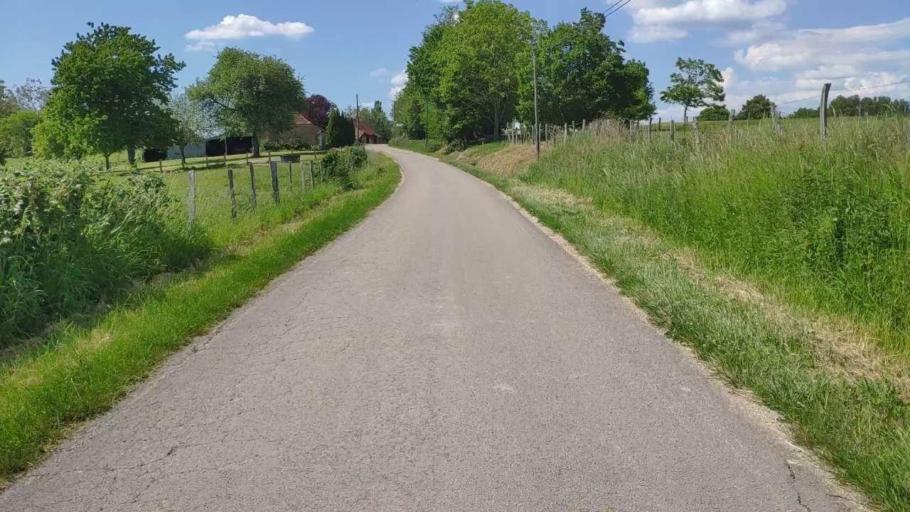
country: FR
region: Franche-Comte
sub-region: Departement du Jura
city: Bletterans
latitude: 46.8186
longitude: 5.4014
